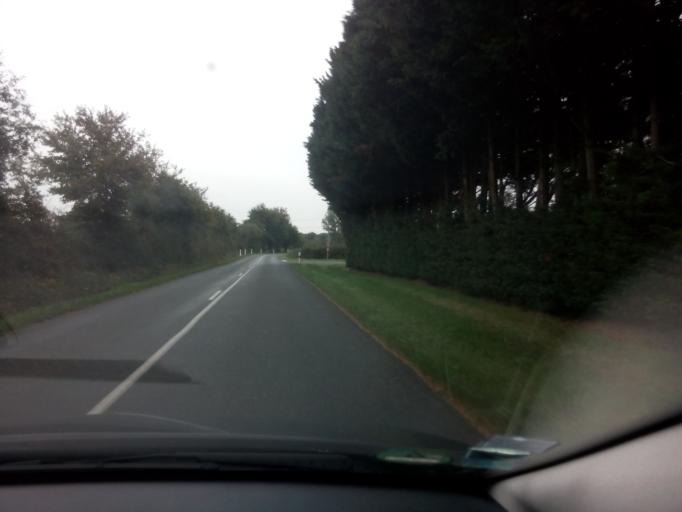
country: FR
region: Pays de la Loire
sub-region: Departement de Maine-et-Loire
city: Etriche
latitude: 47.6183
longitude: -0.4296
